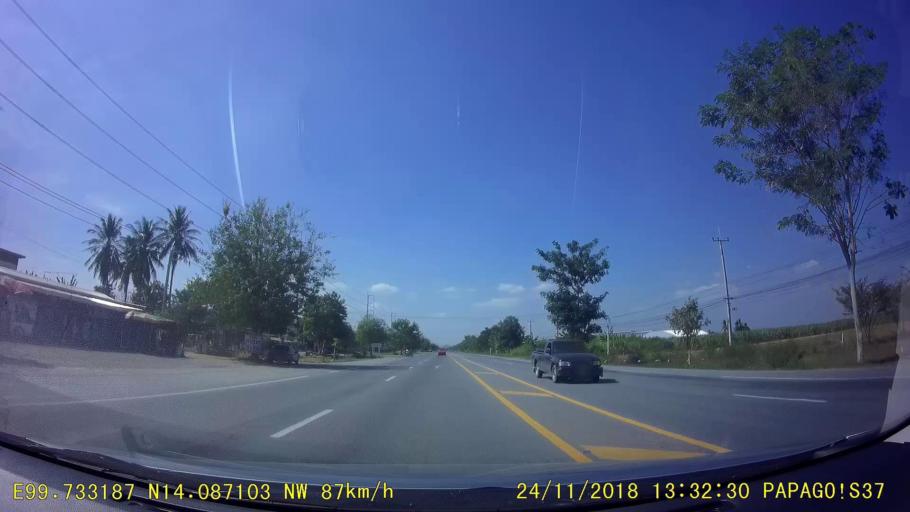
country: TH
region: Kanchanaburi
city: Phanom Thuan
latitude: 14.0859
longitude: 99.7353
